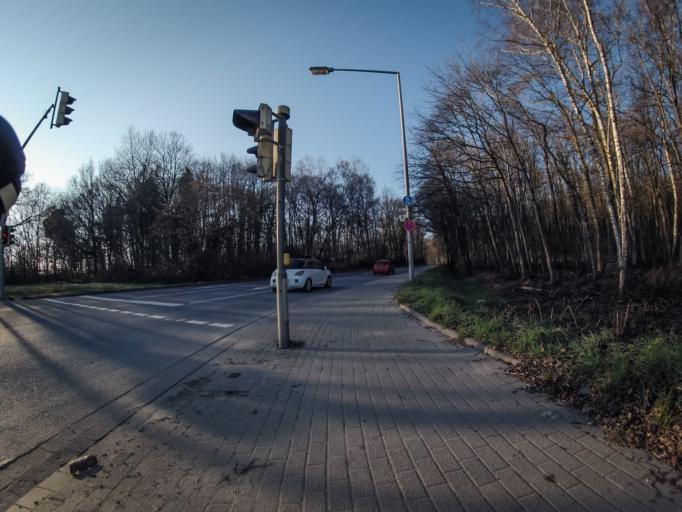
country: DE
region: Lower Saxony
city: Wallenhorst
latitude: 52.3121
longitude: 8.0136
